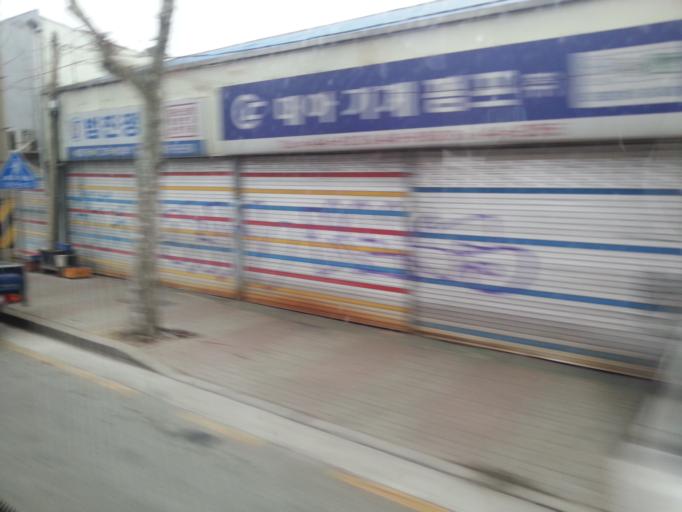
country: KR
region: Gyeonggi-do
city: Anyang-si
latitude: 37.3880
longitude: 126.9340
